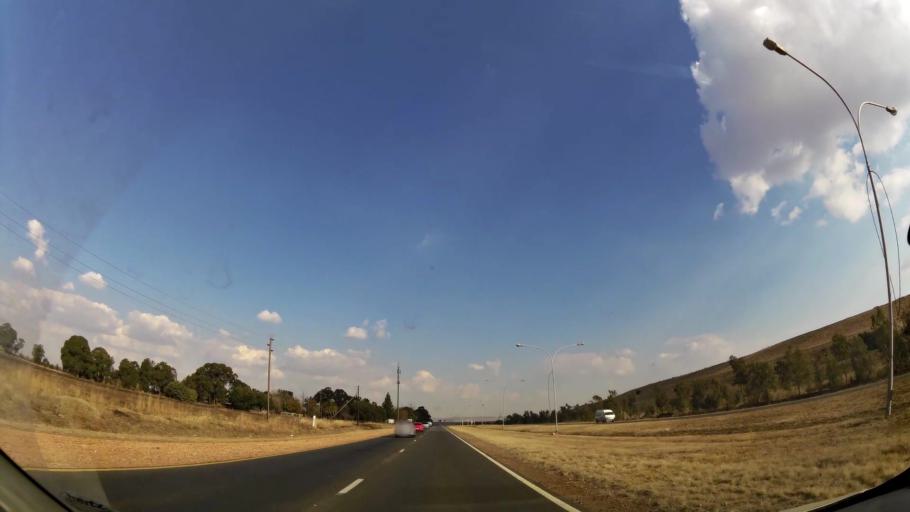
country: ZA
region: Gauteng
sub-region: Ekurhuleni Metropolitan Municipality
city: Springs
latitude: -26.3482
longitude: 28.3418
